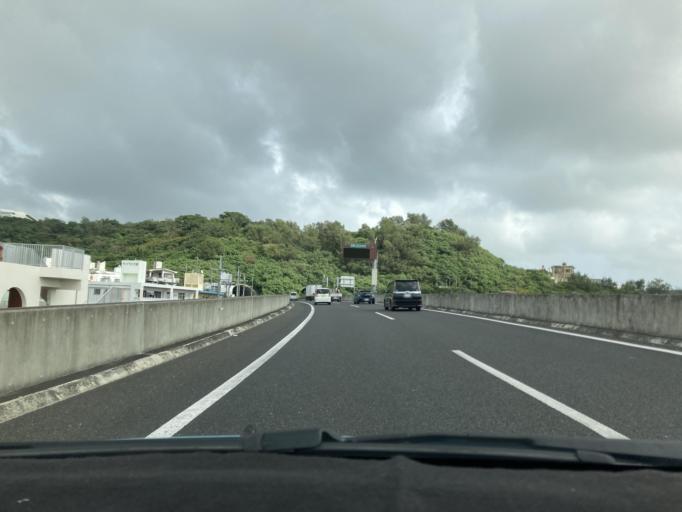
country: JP
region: Okinawa
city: Tomigusuku
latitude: 26.1717
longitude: 127.6780
